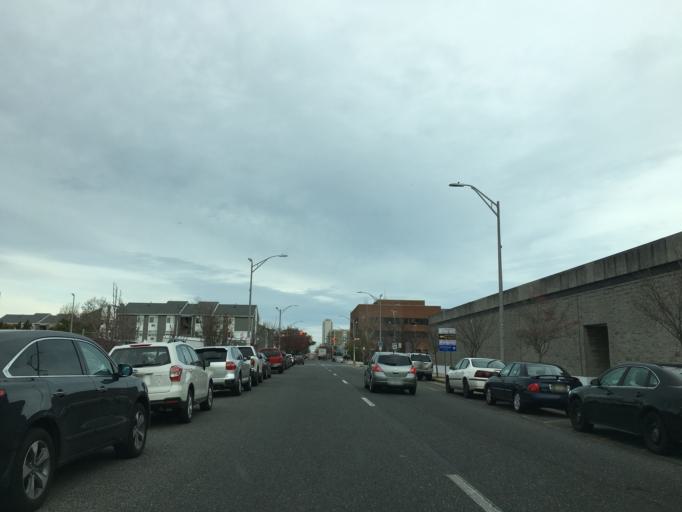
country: US
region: New Jersey
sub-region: Atlantic County
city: Atlantic City
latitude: 39.3637
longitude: -74.4290
